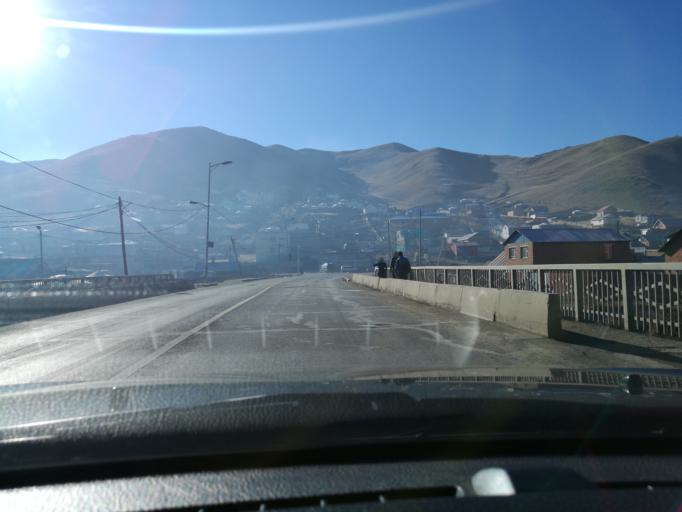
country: MN
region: Ulaanbaatar
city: Ulaanbaatar
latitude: 47.9790
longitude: 106.9388
